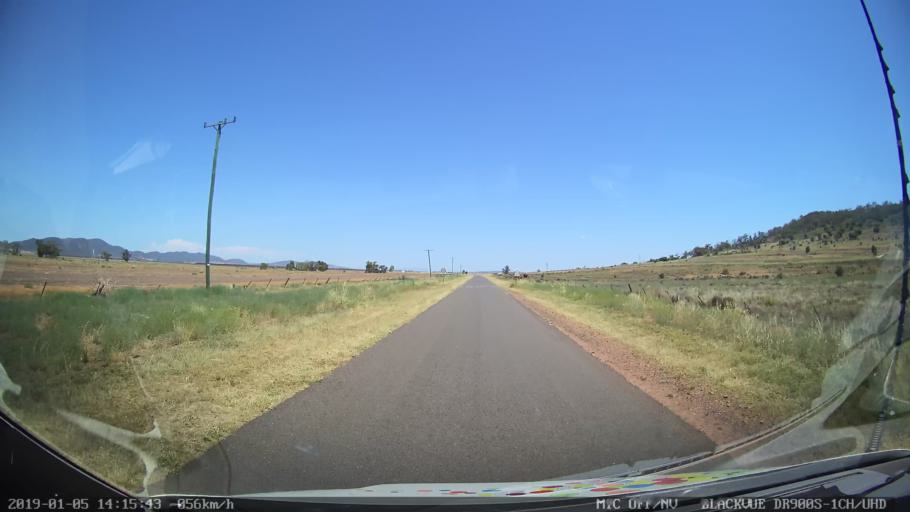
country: AU
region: New South Wales
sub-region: Liverpool Plains
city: Quirindi
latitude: -31.2496
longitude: 150.4715
